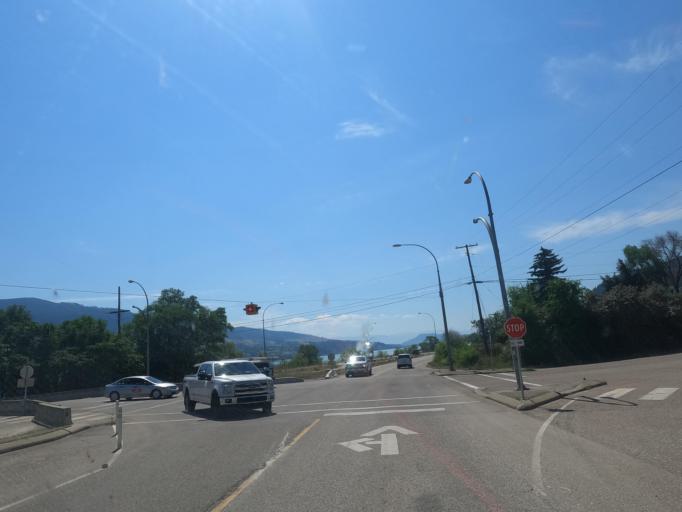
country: CA
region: British Columbia
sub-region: Regional District of North Okanagan
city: Vernon
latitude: 50.1108
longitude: -119.3876
